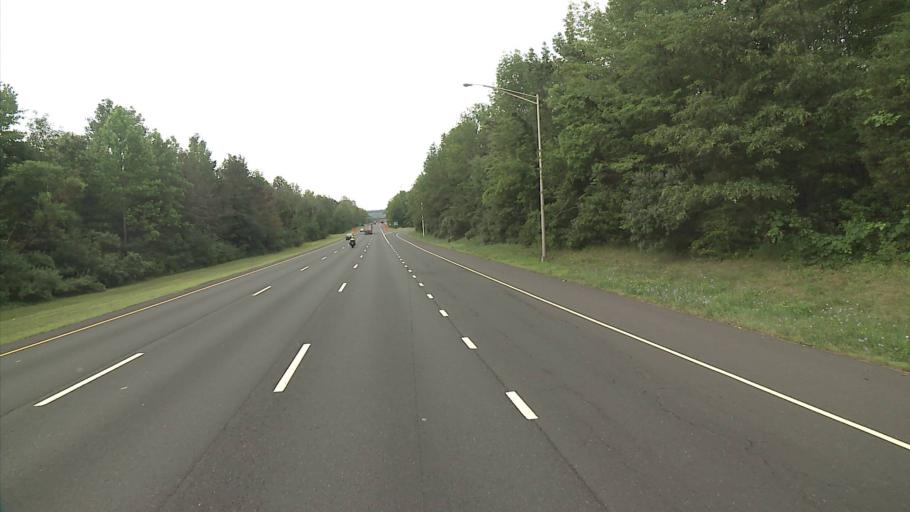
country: US
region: Connecticut
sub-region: Hartford County
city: Plainville
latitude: 41.6815
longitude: -72.8181
